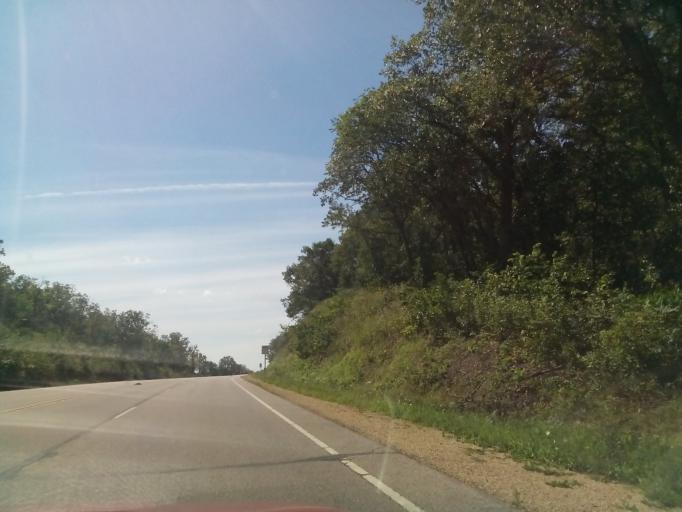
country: US
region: Wisconsin
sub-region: Green County
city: New Glarus
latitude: 42.7882
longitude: -89.6285
